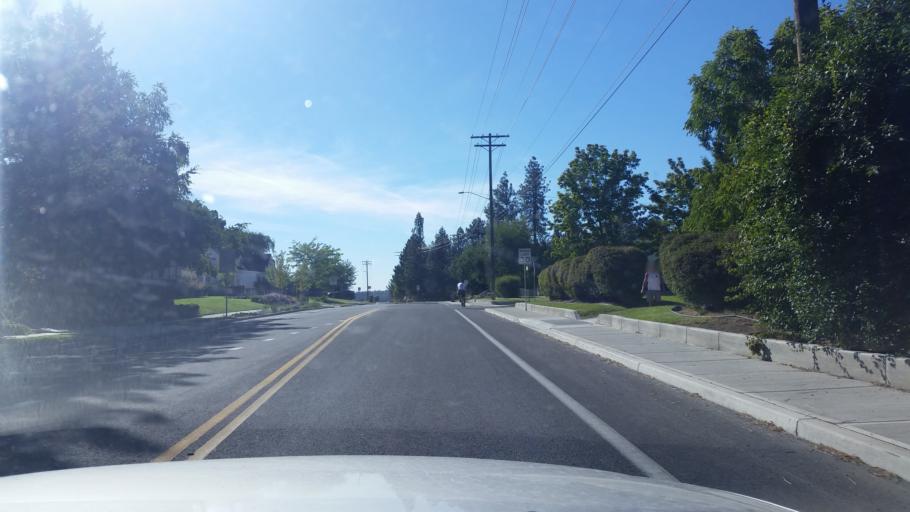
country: US
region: Washington
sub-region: Spokane County
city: Spokane
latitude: 47.6283
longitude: -117.4258
